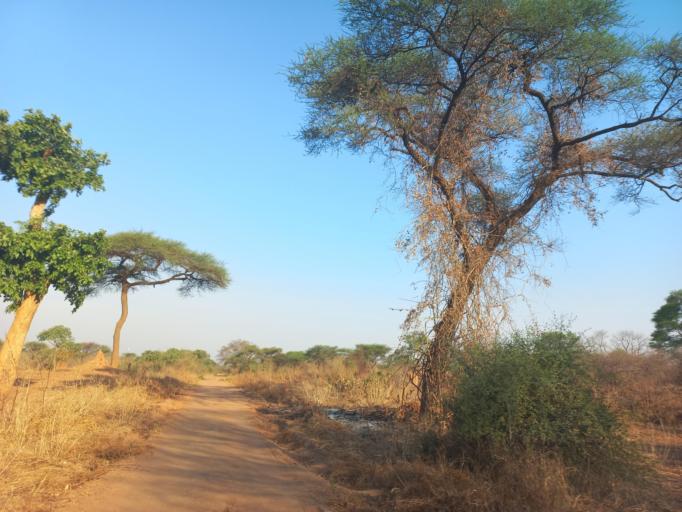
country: ZM
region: Lusaka
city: Luangwa
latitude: -15.4214
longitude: 30.2827
